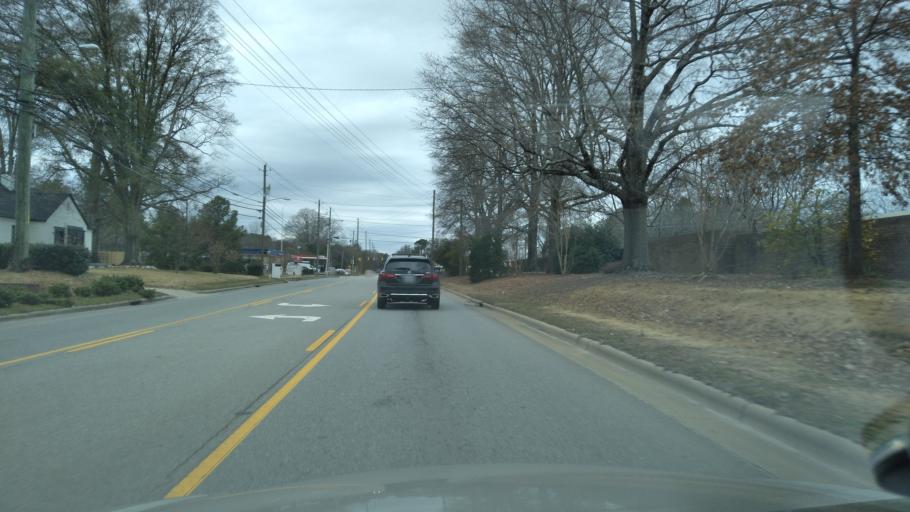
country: US
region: North Carolina
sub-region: Wake County
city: Apex
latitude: 35.7254
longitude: -78.8488
